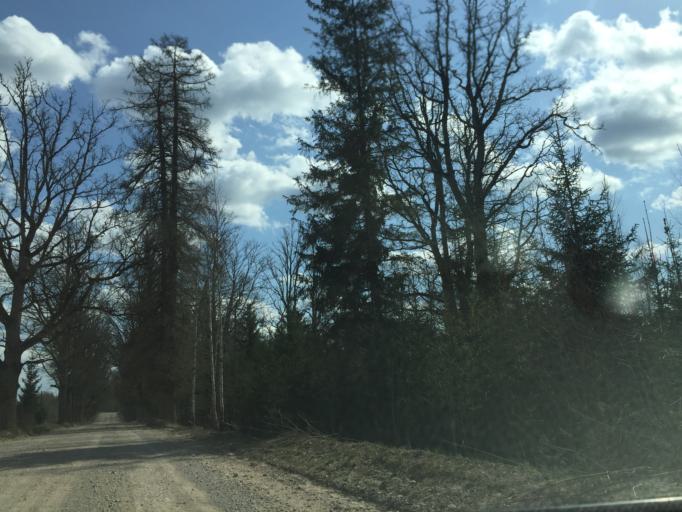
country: LV
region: Skriveri
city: Skriveri
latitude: 56.7525
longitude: 25.0808
